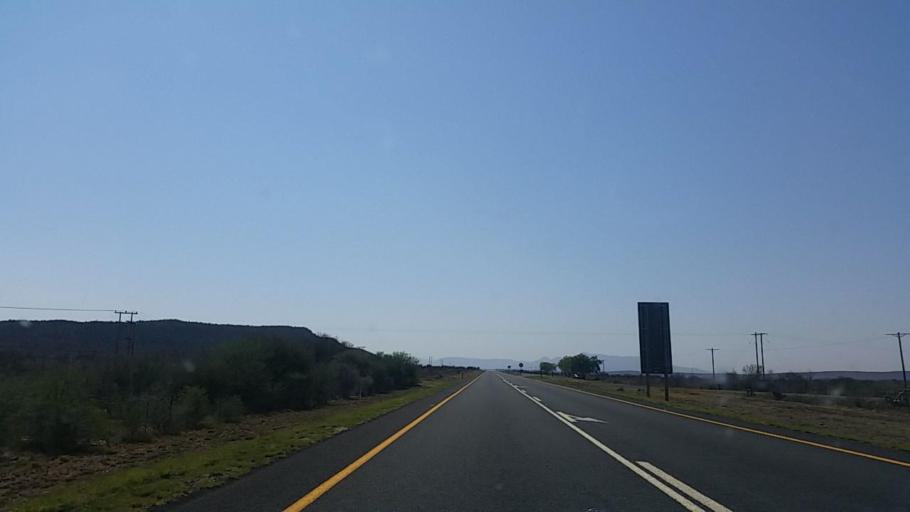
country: ZA
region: Eastern Cape
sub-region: Cacadu District Municipality
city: Graaff-Reinet
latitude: -32.3419
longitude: 24.3797
